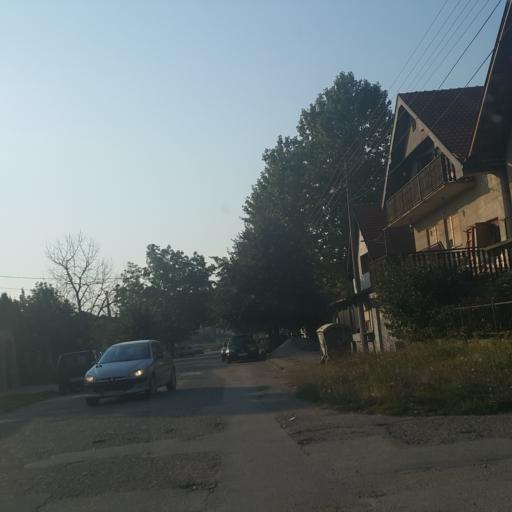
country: RS
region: Central Serbia
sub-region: Zajecarski Okrug
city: Zajecar
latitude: 43.9063
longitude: 22.2594
